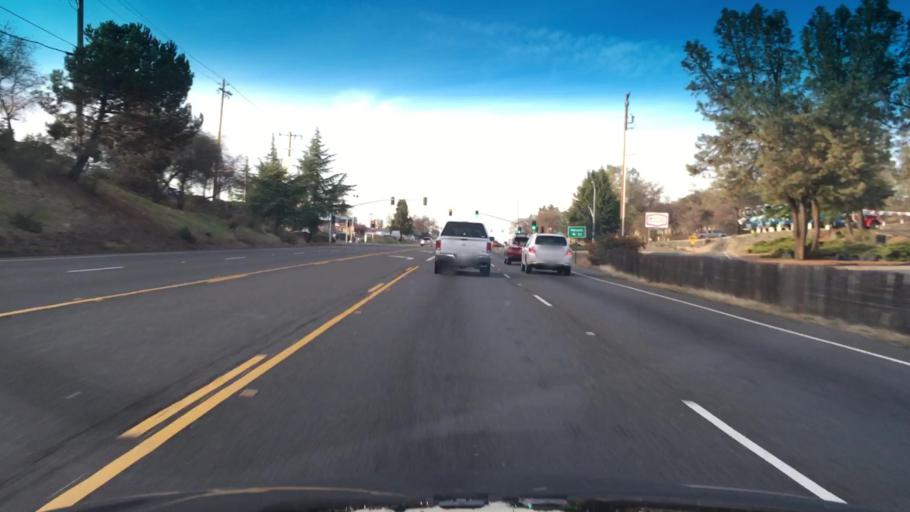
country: US
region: California
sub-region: Placer County
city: North Auburn
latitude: 38.9176
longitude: -121.0805
